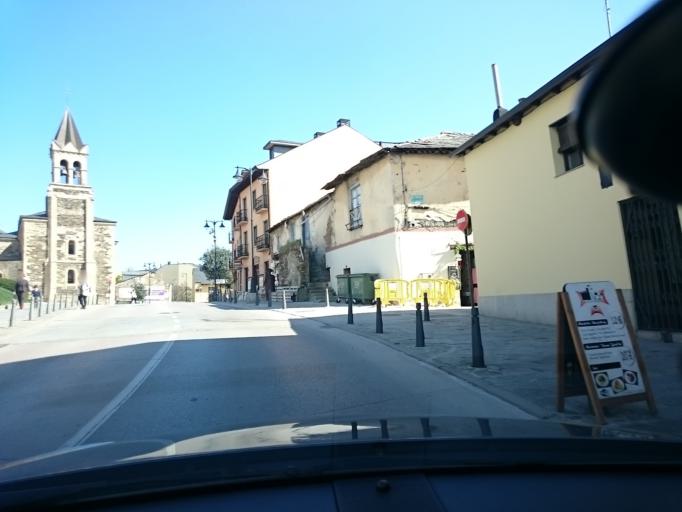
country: ES
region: Castille and Leon
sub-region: Provincia de Leon
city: Ponferrada
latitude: 42.5430
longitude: -6.5941
